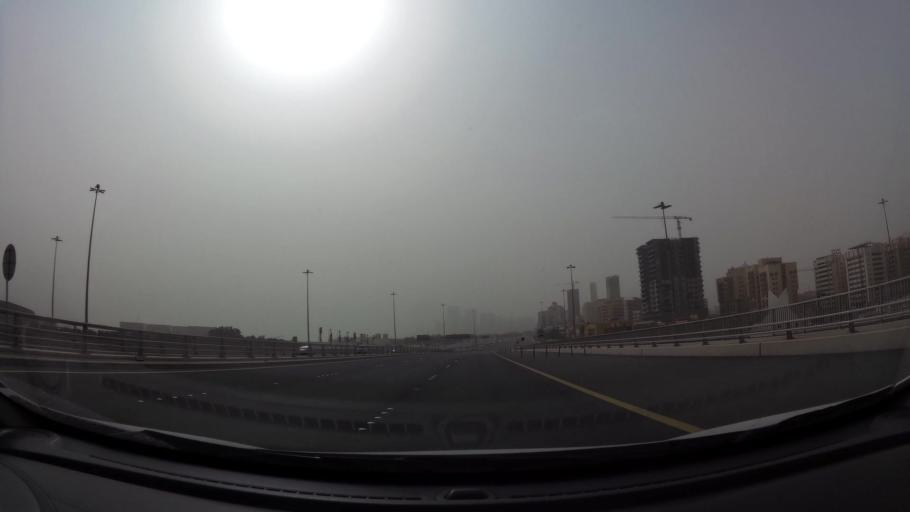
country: BH
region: Muharraq
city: Al Muharraq
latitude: 26.2421
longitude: 50.5939
